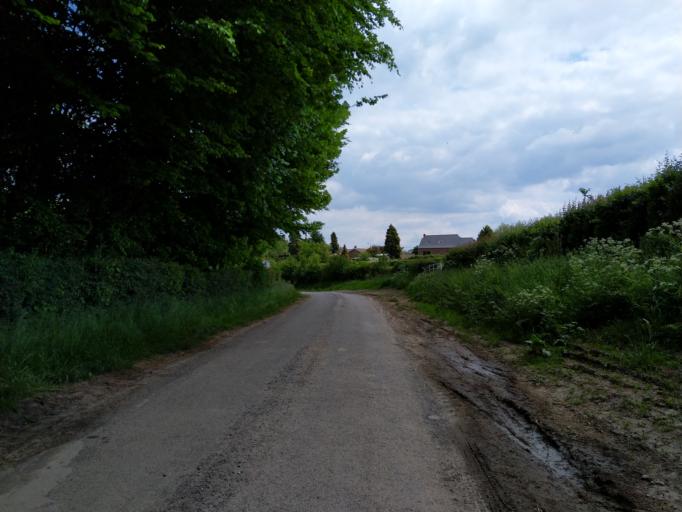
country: FR
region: Nord-Pas-de-Calais
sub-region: Departement du Nord
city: Le Quesnoy
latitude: 50.2453
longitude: 3.6736
